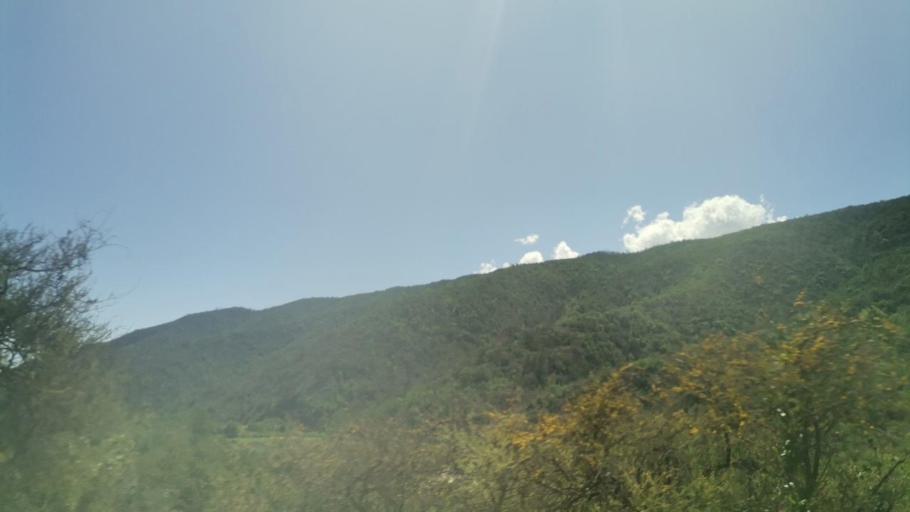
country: CL
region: Valparaiso
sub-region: Provincia de Marga Marga
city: Villa Alemana
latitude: -33.1923
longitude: -71.2824
